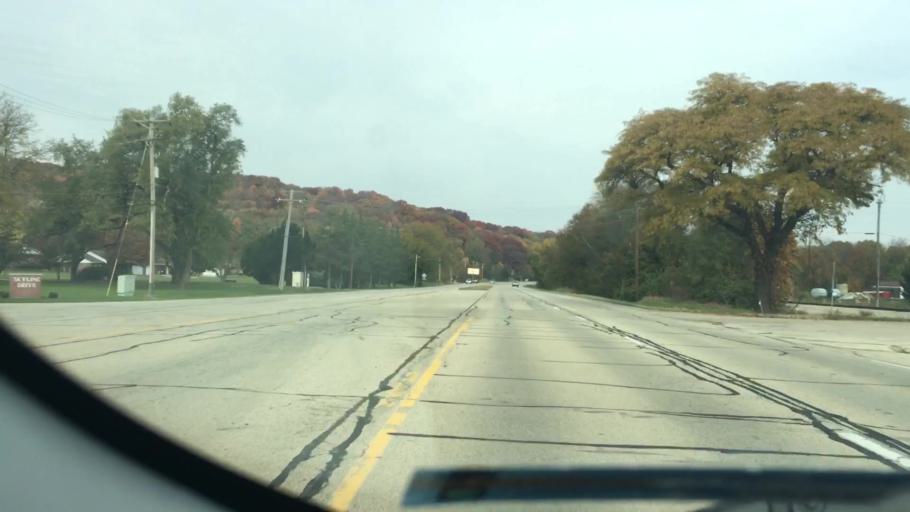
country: US
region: Illinois
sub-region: Peoria County
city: Peoria Heights
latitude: 40.7724
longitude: -89.5738
